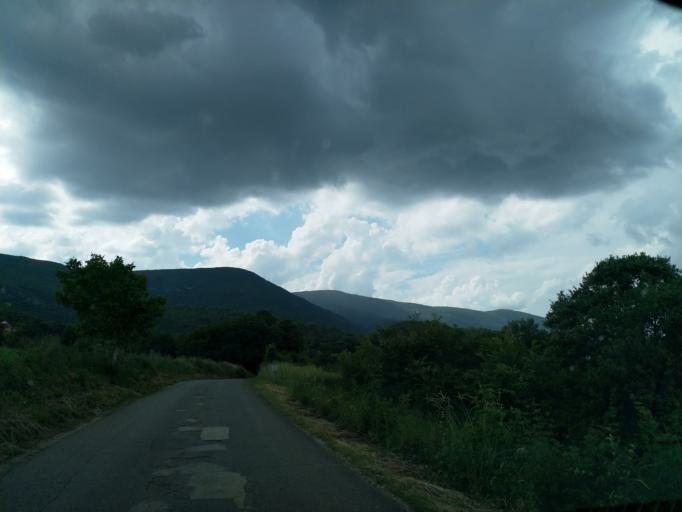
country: RS
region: Central Serbia
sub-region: Borski Okrug
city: Bor
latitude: 44.0270
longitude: 21.9705
